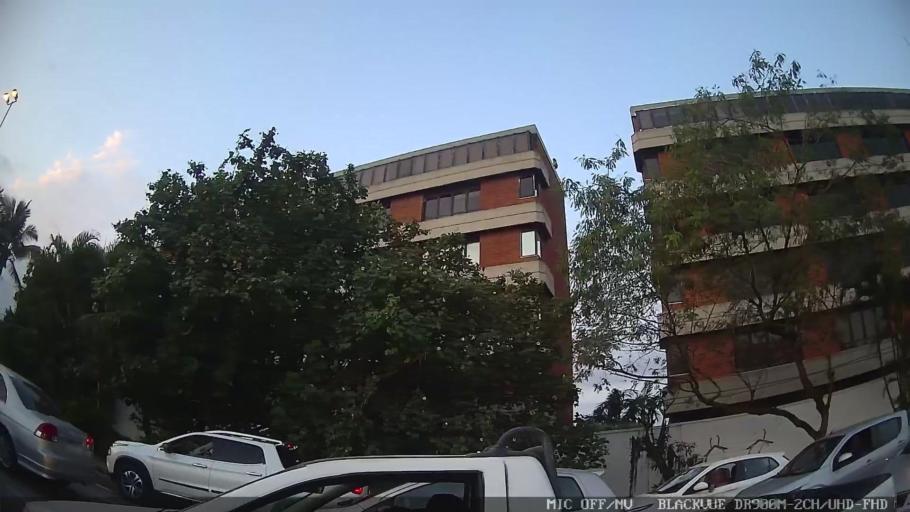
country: BR
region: Sao Paulo
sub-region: Guaruja
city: Guaruja
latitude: -23.9880
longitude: -46.2876
